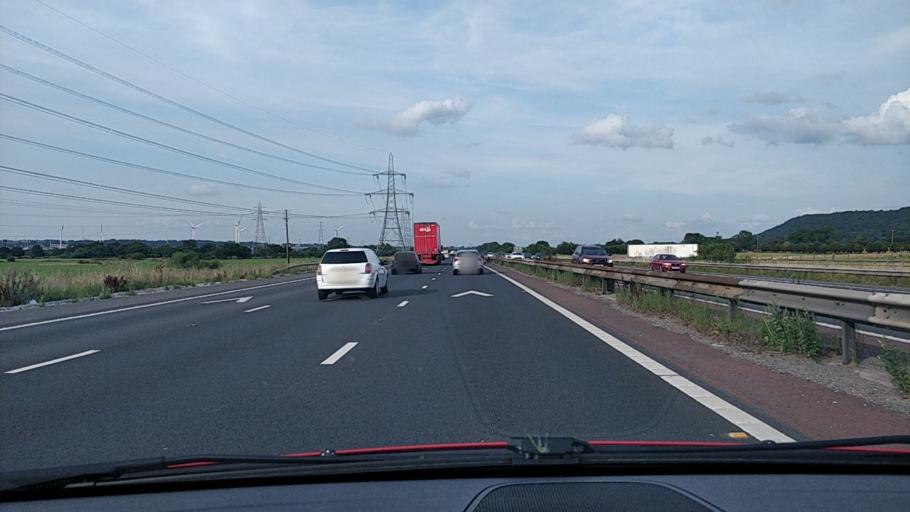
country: GB
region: England
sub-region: Cheshire West and Chester
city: Helsby
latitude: 53.2818
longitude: -2.7643
